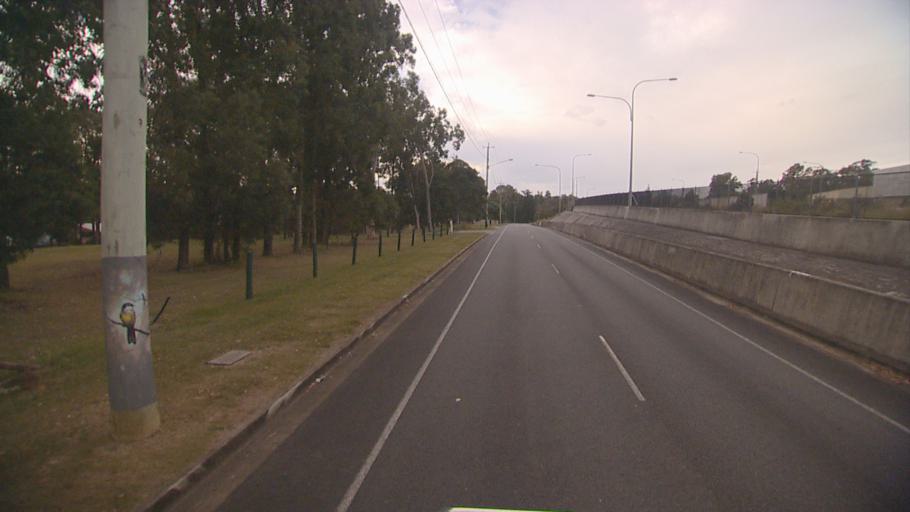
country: AU
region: Queensland
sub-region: Logan
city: Park Ridge South
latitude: -27.7158
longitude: 153.0332
